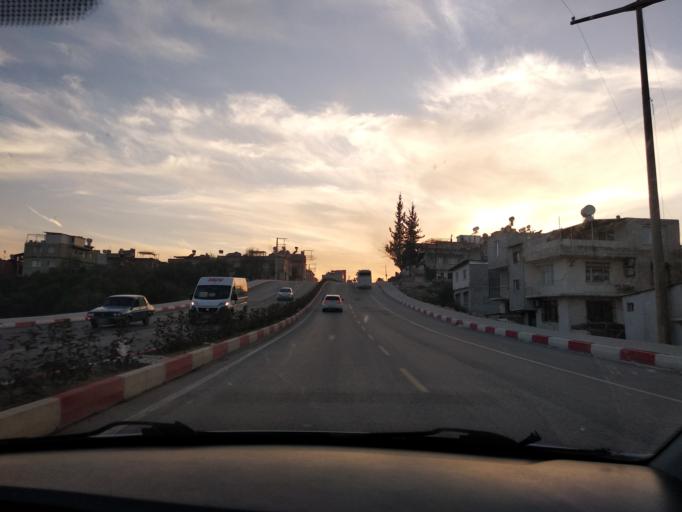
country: TR
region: Mersin
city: Mercin
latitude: 36.8279
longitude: 34.6083
